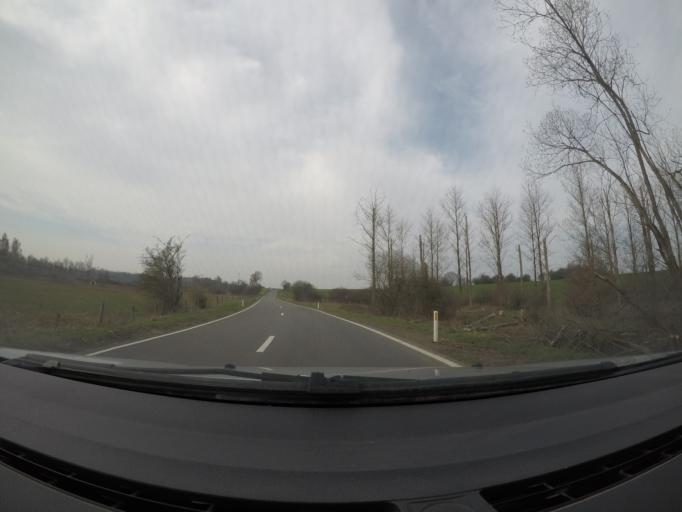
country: BE
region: Wallonia
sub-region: Province du Luxembourg
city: Tintigny
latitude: 49.7067
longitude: 5.4374
